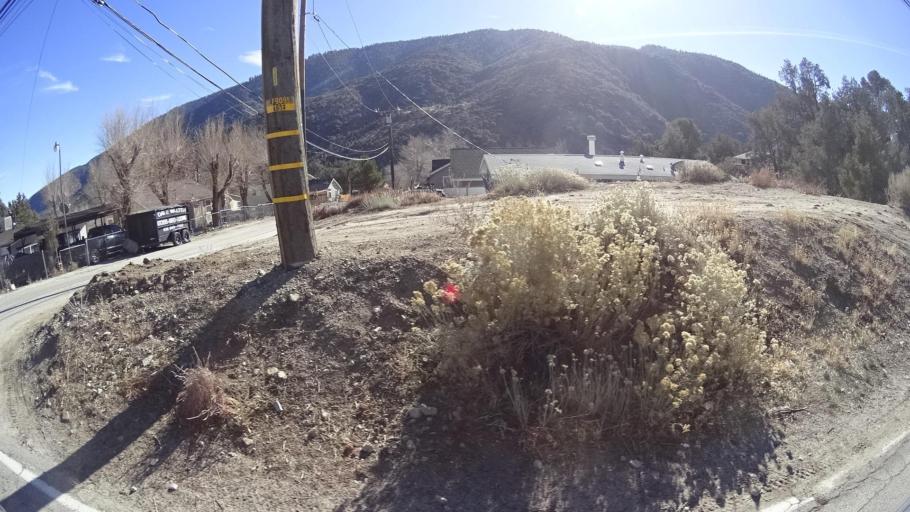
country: US
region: California
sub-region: Kern County
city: Frazier Park
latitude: 34.8230
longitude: -118.9603
